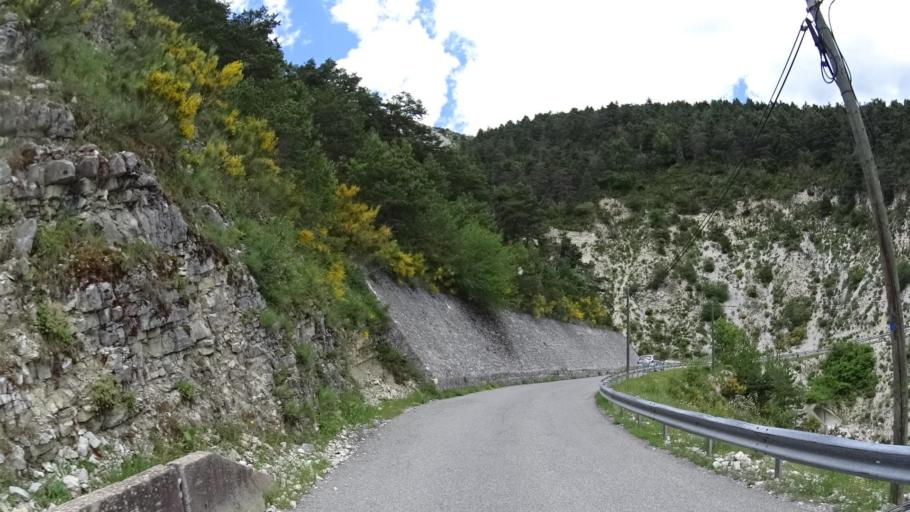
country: FR
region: Provence-Alpes-Cote d'Azur
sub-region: Departement des Alpes-de-Haute-Provence
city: Annot
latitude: 44.0247
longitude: 6.6167
